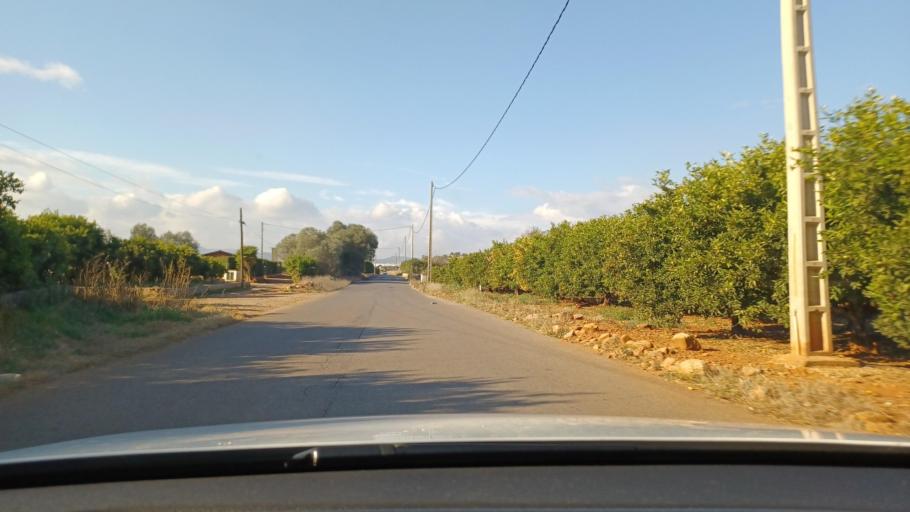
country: ES
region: Valencia
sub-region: Provincia de Castello
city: Betxi
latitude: 39.9487
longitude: -0.2248
